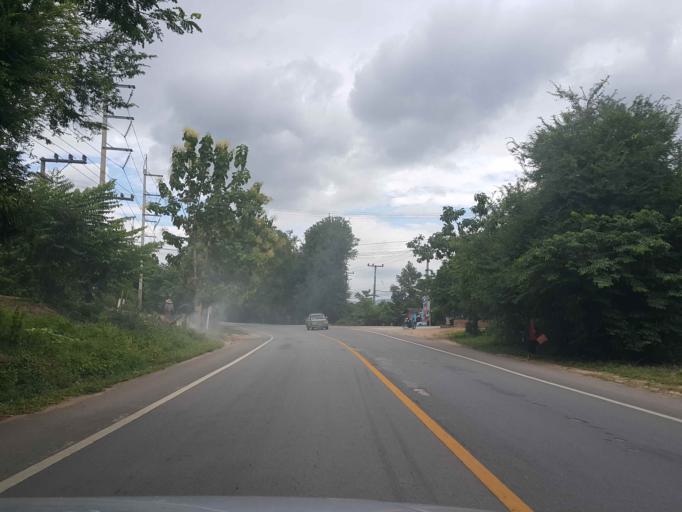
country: TH
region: Lamphun
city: Thung Hua Chang
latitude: 17.9708
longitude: 98.8844
